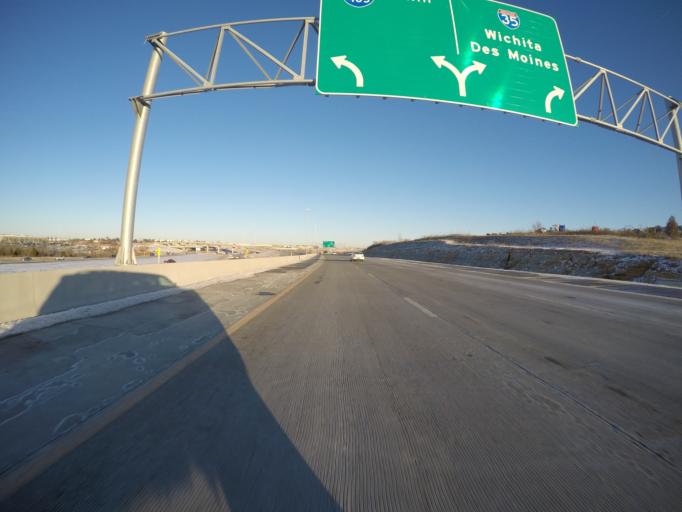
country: US
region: Kansas
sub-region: Johnson County
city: Lenexa
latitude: 38.9412
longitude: -94.7789
